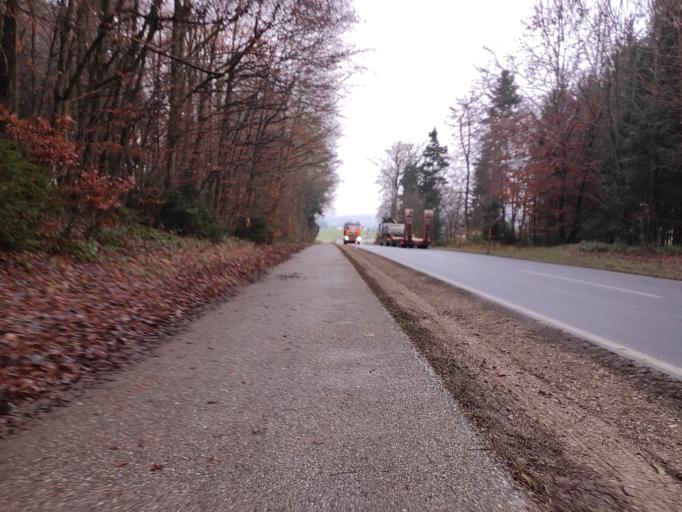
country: AT
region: Salzburg
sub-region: Politischer Bezirk Salzburg-Umgebung
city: Seekirchen am Wallersee
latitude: 47.9080
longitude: 13.1169
